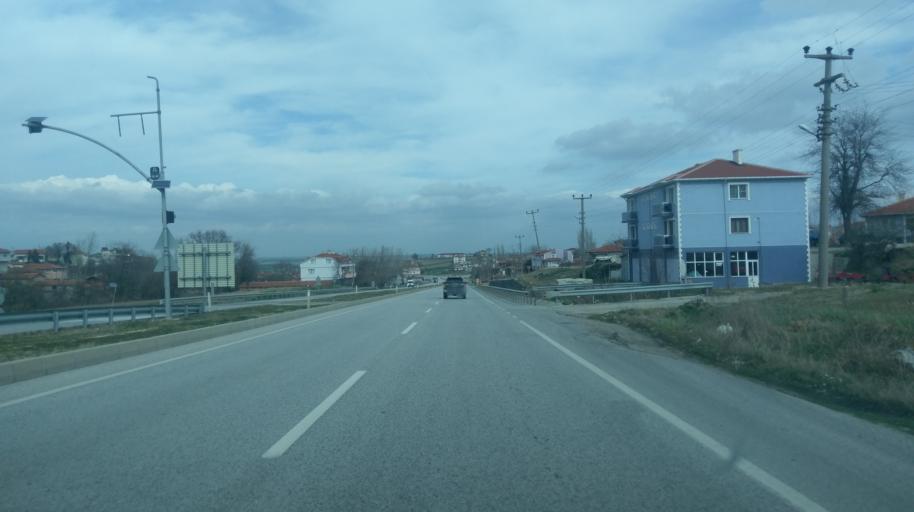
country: TR
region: Edirne
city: Kircasalih
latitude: 41.3927
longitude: 26.8034
